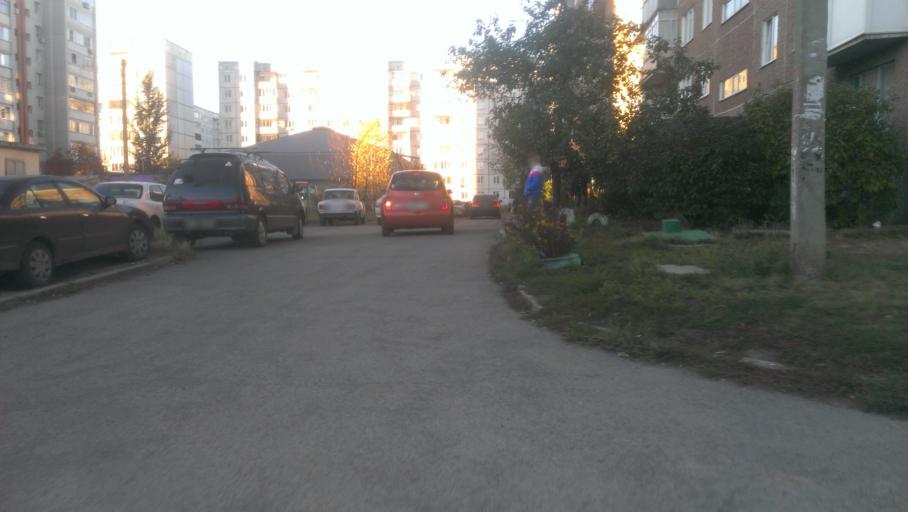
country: RU
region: Altai Krai
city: Novosilikatnyy
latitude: 53.3408
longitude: 83.6722
